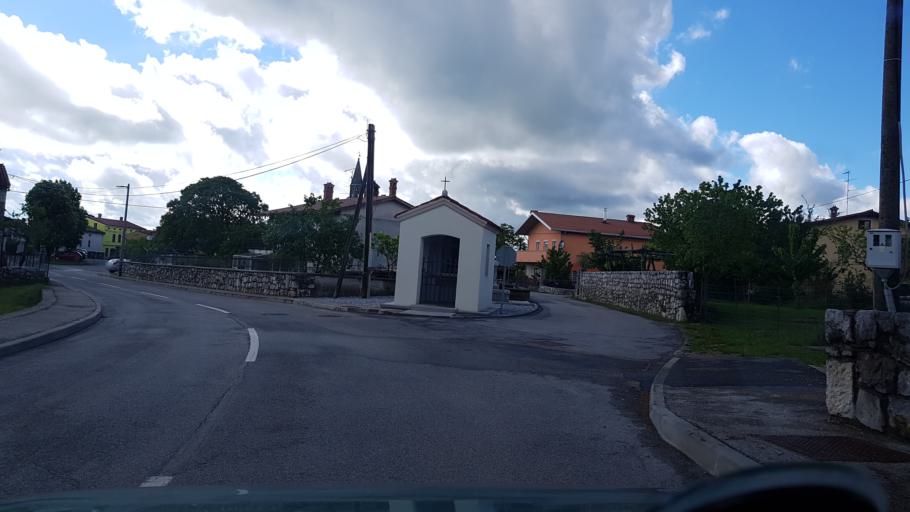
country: IT
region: Friuli Venezia Giulia
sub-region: Provincia di Gorizia
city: Doberdo del Lago
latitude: 45.8509
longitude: 13.5852
